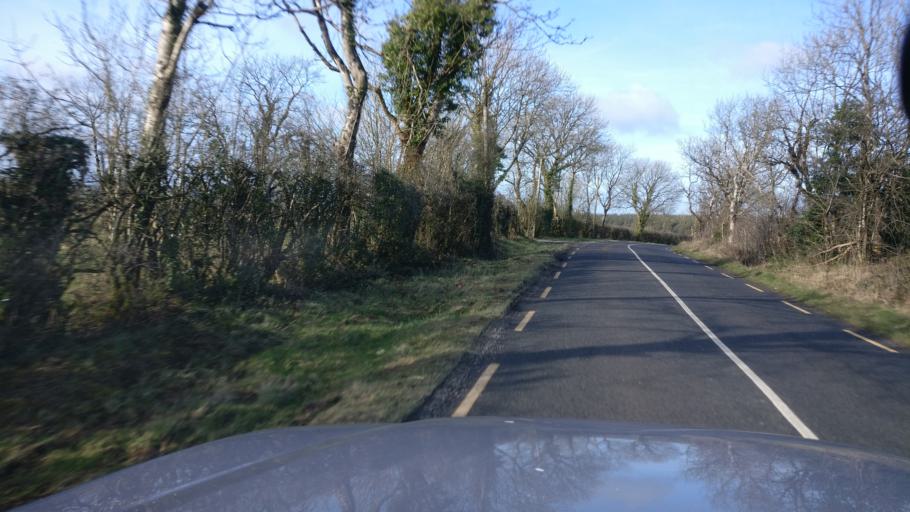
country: IE
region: Leinster
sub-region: Laois
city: Stradbally
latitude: 52.9169
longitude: -7.1872
